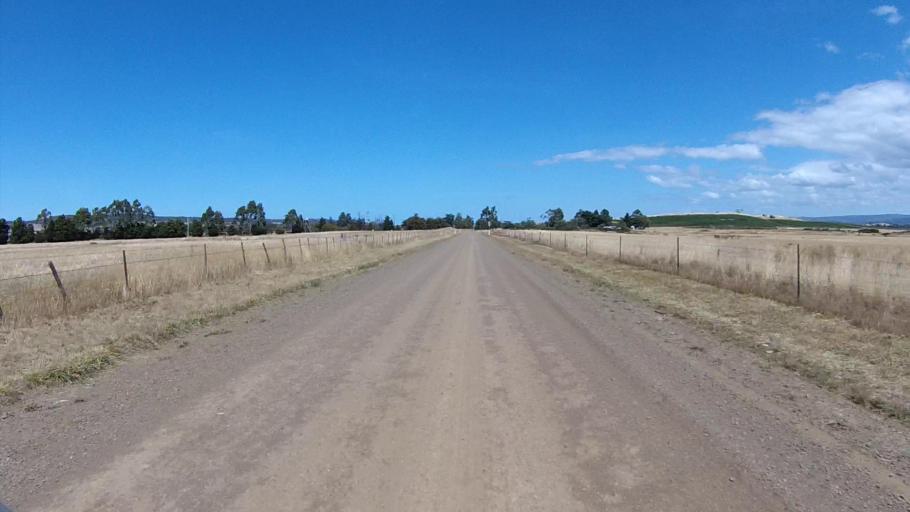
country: AU
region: Tasmania
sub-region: Break O'Day
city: St Helens
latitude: -41.9993
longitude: 148.0673
